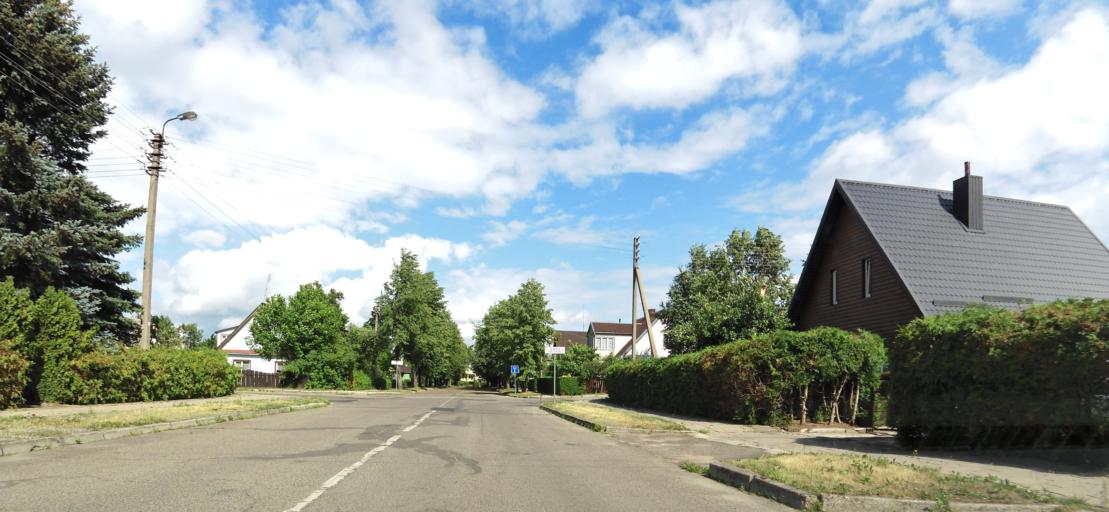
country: LT
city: Kupiskis
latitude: 55.8412
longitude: 24.9797
